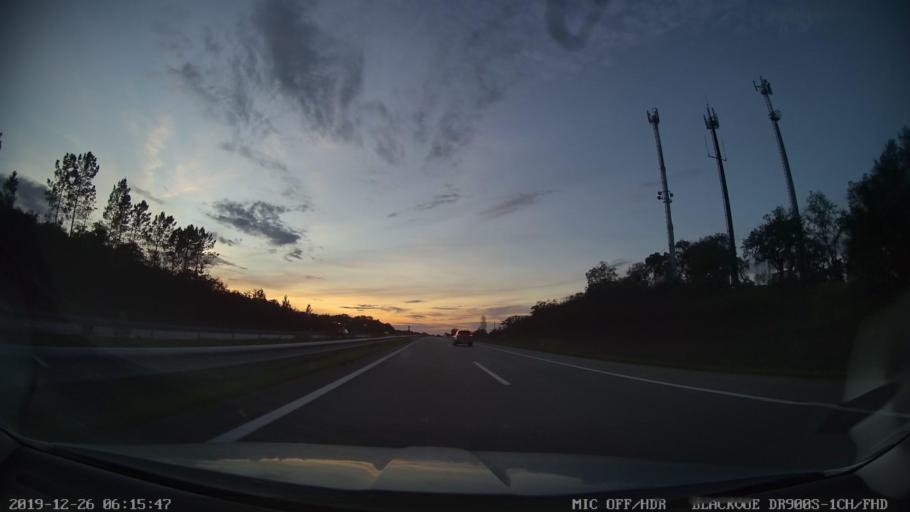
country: PT
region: Evora
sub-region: Montemor-O-Novo
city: Montemor-o-Novo
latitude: 38.6362
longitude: -8.3175
